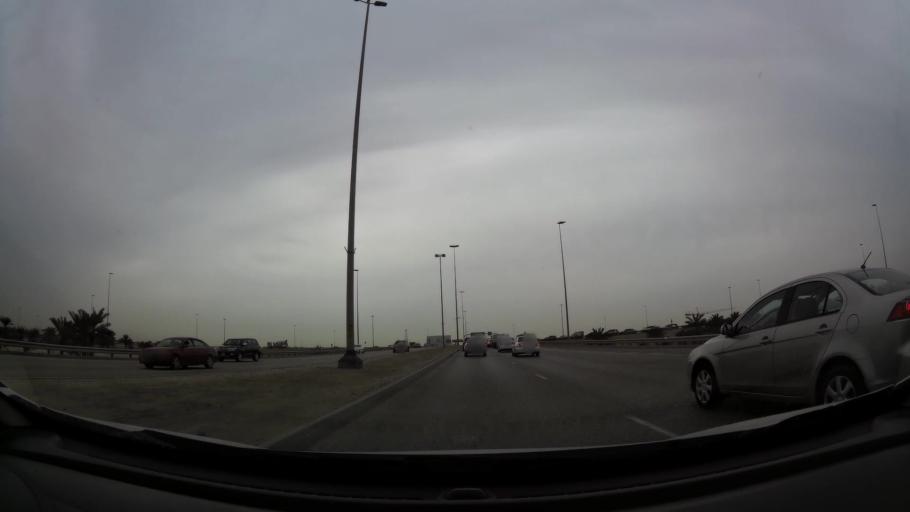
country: BH
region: Manama
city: Jidd Hafs
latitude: 26.1986
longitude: 50.5341
